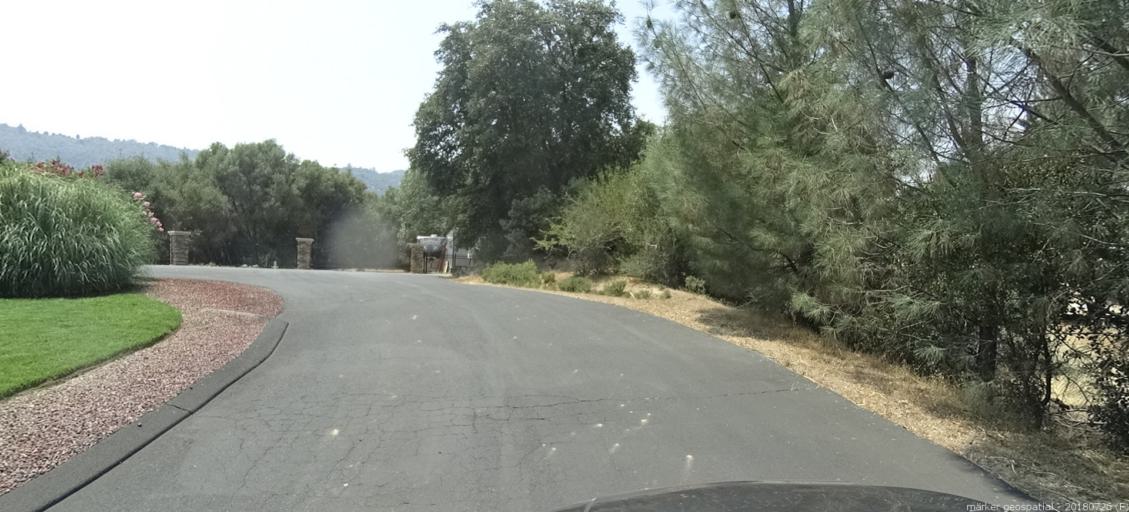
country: US
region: California
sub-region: Madera County
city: Oakhurst
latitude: 37.3166
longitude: -119.6488
